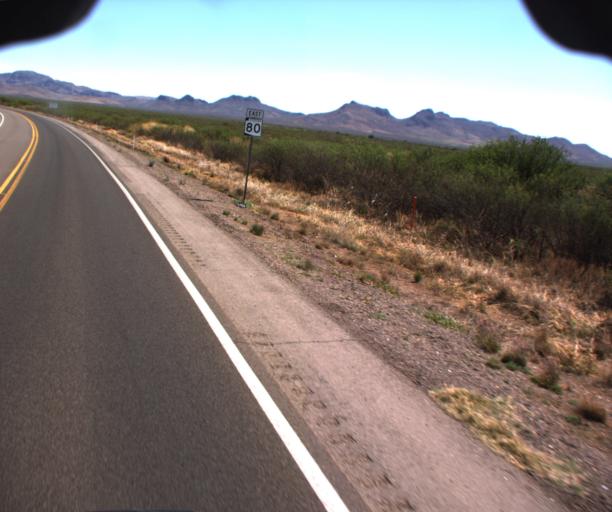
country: US
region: Arizona
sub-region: Cochise County
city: Douglas
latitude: 31.3760
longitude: -109.5226
